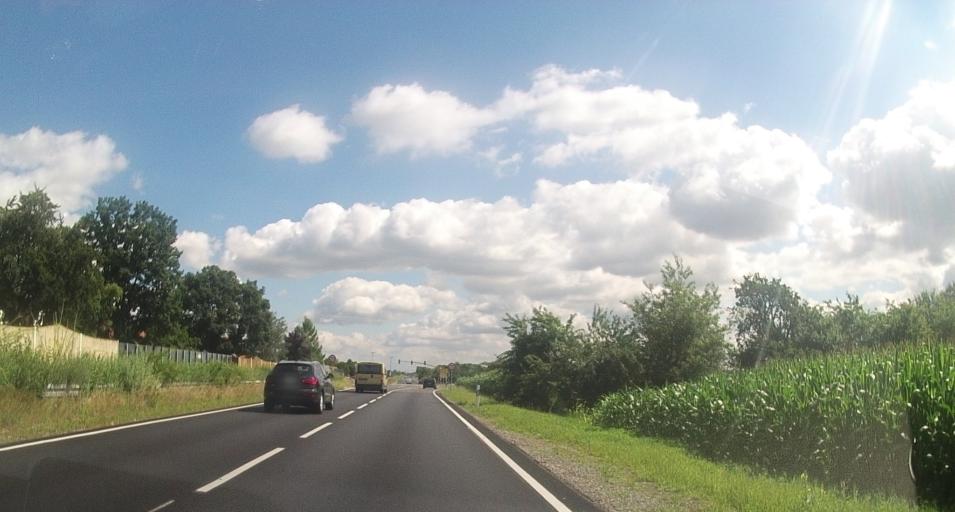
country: DE
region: Baden-Wuerttemberg
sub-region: Karlsruhe Region
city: Rheinstetten
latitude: 48.9726
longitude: 8.3158
